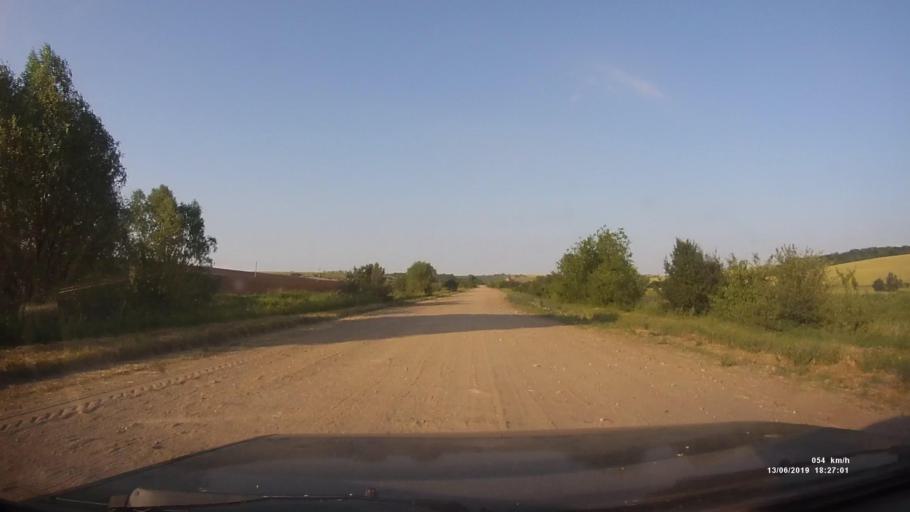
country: RU
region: Rostov
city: Kazanskaya
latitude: 49.8527
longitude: 41.3187
